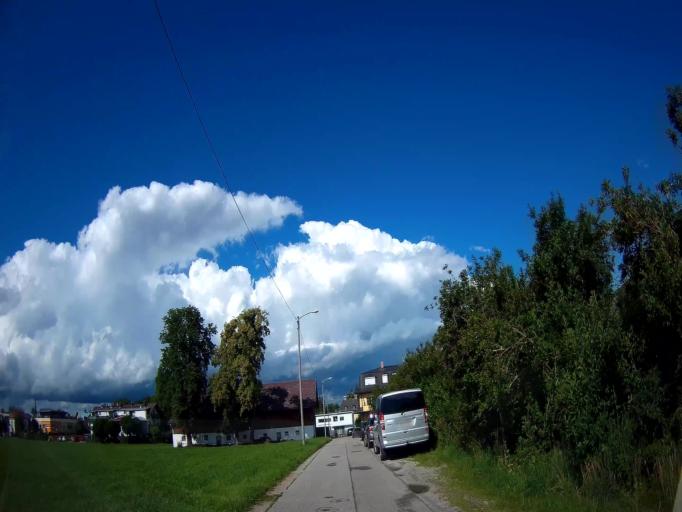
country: AT
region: Salzburg
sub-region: Salzburg Stadt
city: Salzburg
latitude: 47.7974
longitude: 13.0169
